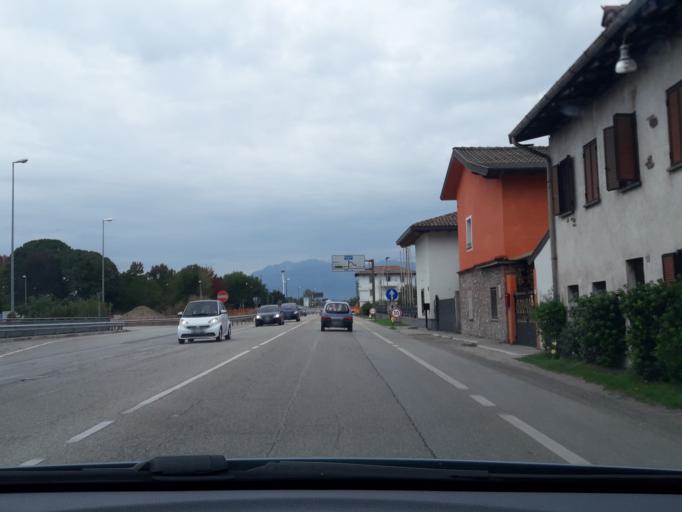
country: IT
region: Friuli Venezia Giulia
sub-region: Provincia di Udine
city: Tavagnacco
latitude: 46.1148
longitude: 13.2271
